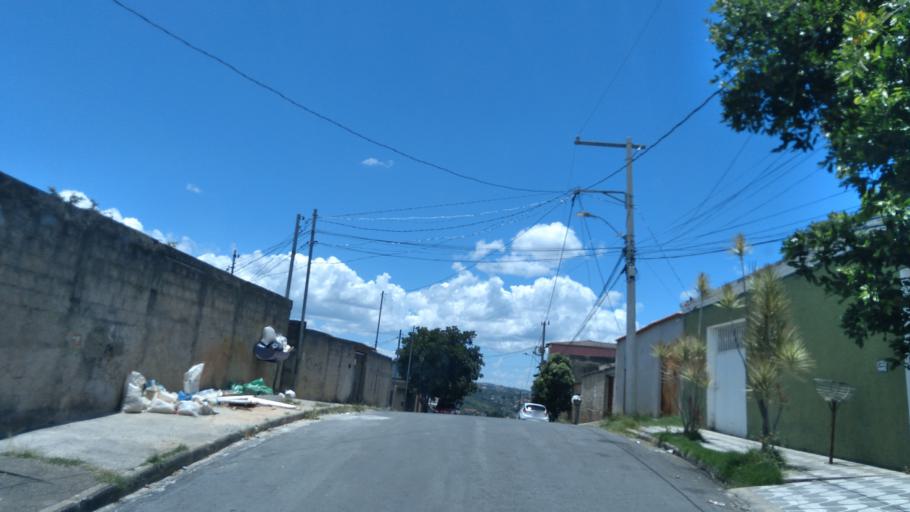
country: BR
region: Minas Gerais
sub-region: Santa Luzia
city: Santa Luzia
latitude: -19.8402
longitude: -43.8964
